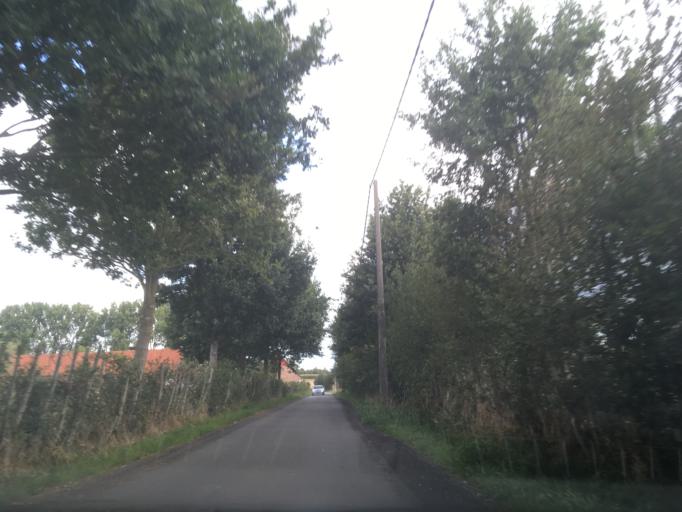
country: BE
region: Flanders
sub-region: Provincie West-Vlaanderen
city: Kortemark
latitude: 51.0180
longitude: 3.0556
